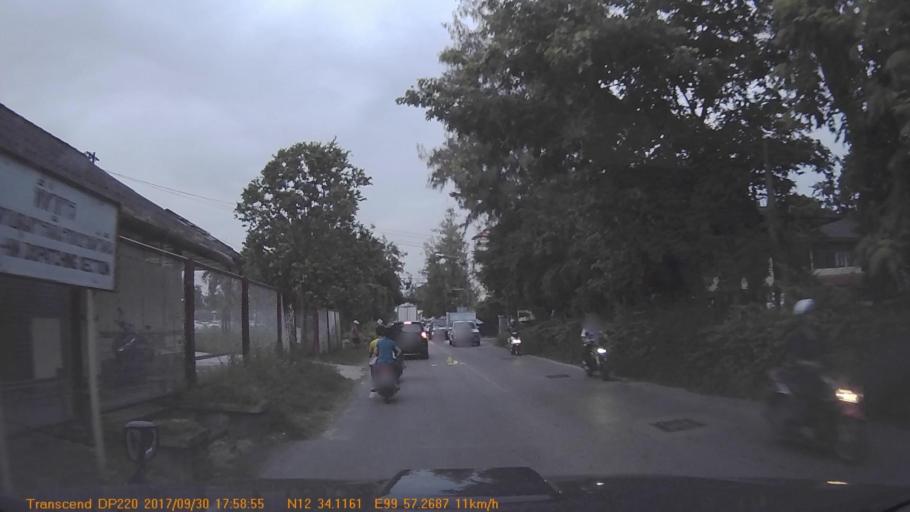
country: TH
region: Prachuap Khiri Khan
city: Hua Hin
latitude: 12.5687
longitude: 99.9545
